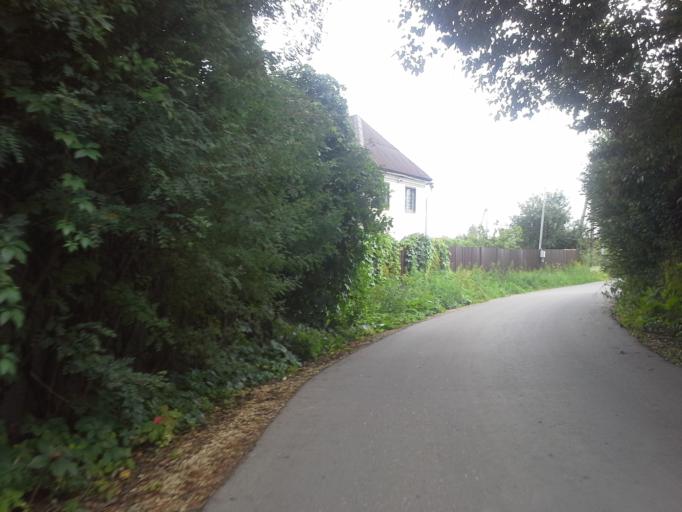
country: RU
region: Moskovskaya
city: Poselok Mar'ino
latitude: 55.5225
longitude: 37.3193
